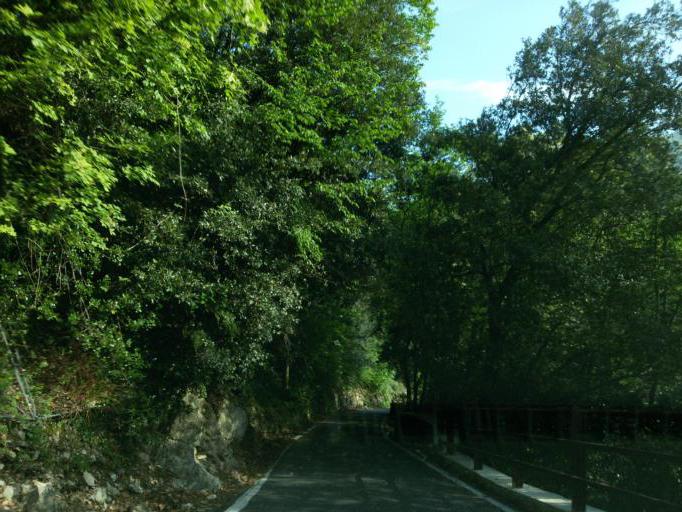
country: IT
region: Liguria
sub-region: Provincia di Genova
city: Piccarello
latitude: 44.4489
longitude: 8.9908
